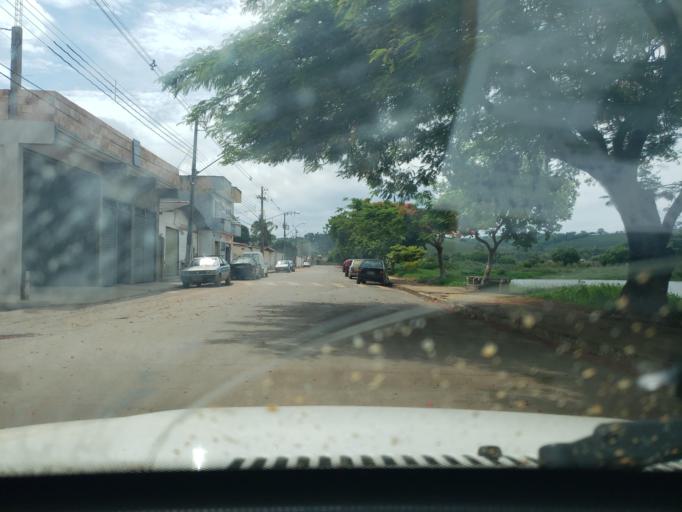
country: BR
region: Minas Gerais
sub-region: Boa Esperanca
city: Boa Esperanca
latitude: -21.0814
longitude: -45.5732
